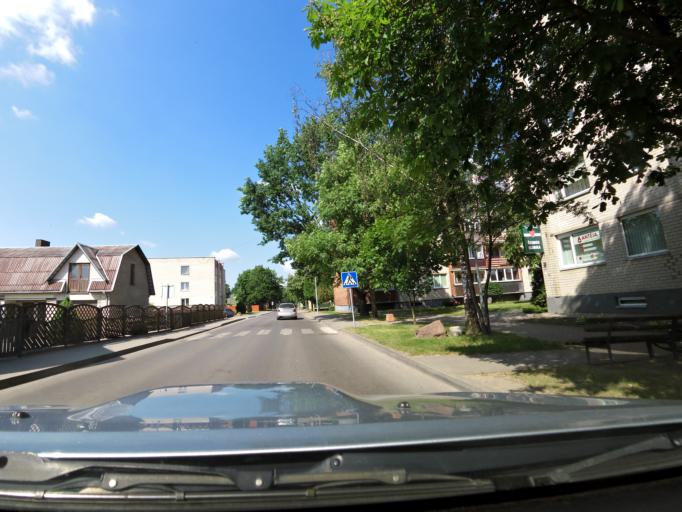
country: LT
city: Vilkaviskis
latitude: 54.6521
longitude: 23.0338
